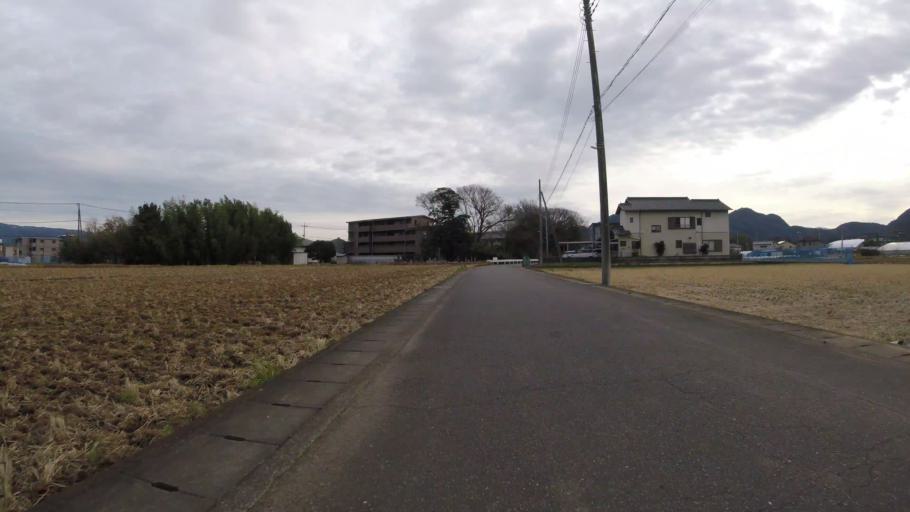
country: JP
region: Shizuoka
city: Mishima
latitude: 35.0911
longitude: 138.9107
